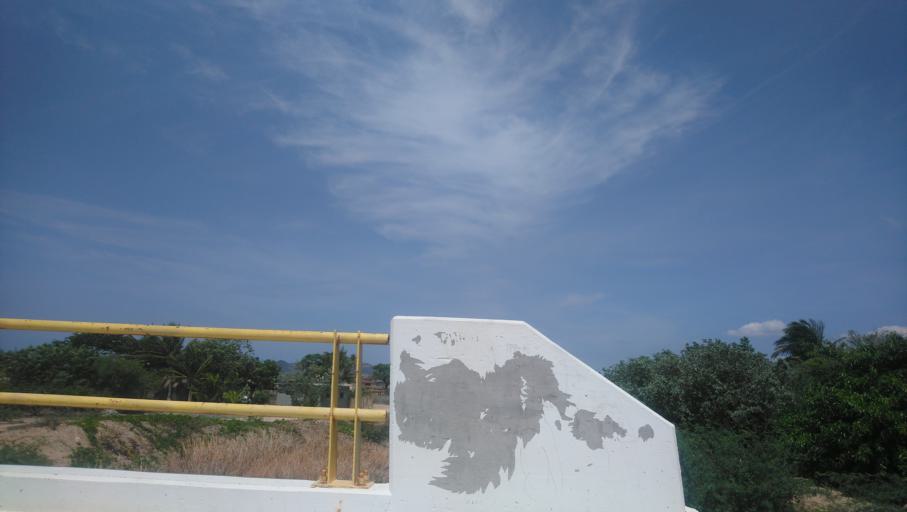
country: MX
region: Oaxaca
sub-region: Salina Cruz
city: Salina Cruz
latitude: 16.1919
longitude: -95.1190
